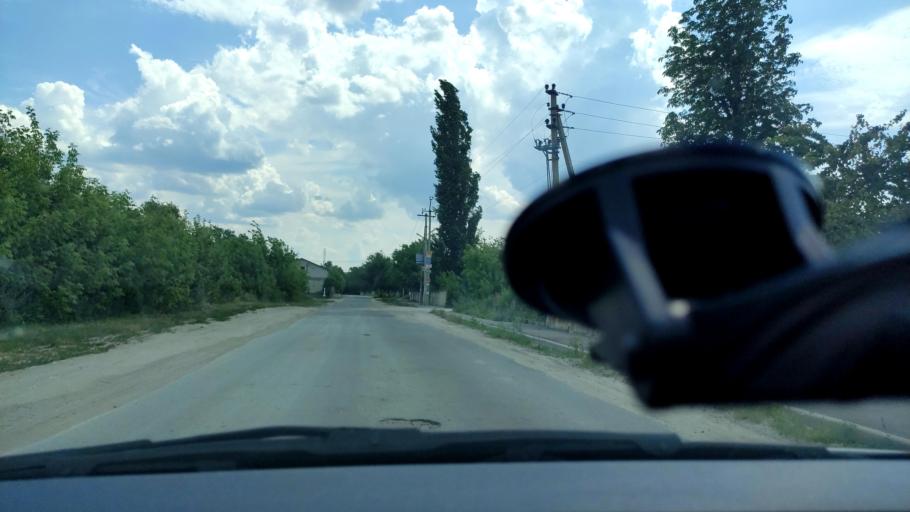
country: RU
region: Voronezj
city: Ramon'
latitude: 51.9043
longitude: 39.3327
